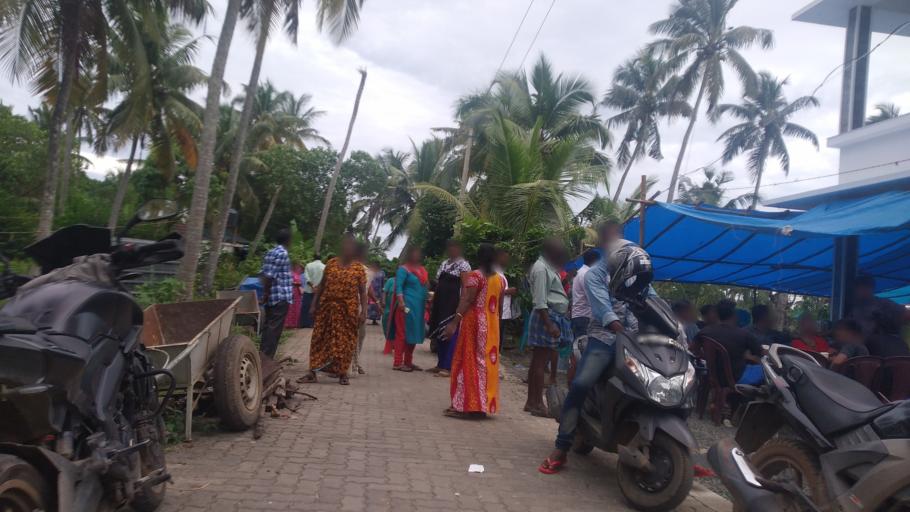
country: IN
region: Kerala
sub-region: Ernakulam
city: Cochin
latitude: 9.8713
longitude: 76.2751
